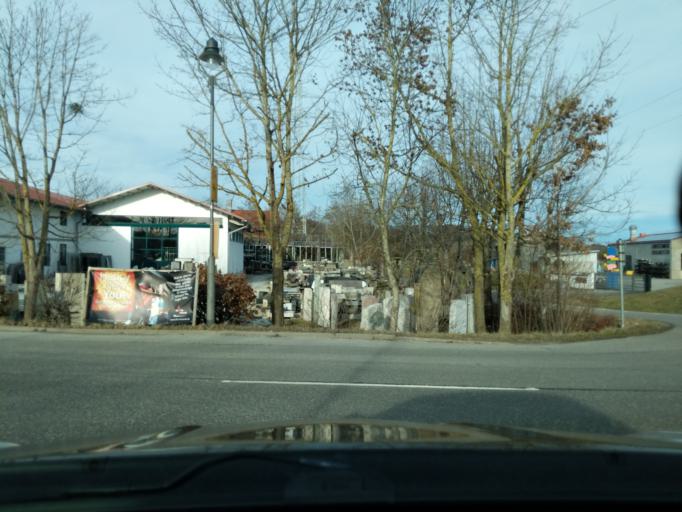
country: DE
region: Bavaria
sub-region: Upper Bavaria
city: Ebersberg
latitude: 48.0794
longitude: 11.9876
